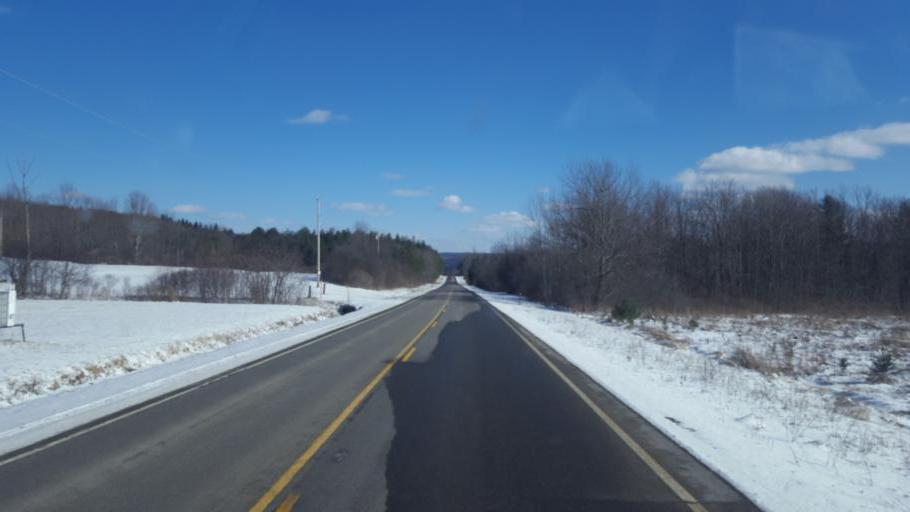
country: US
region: New York
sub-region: Allegany County
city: Friendship
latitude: 42.1841
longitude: -78.0840
